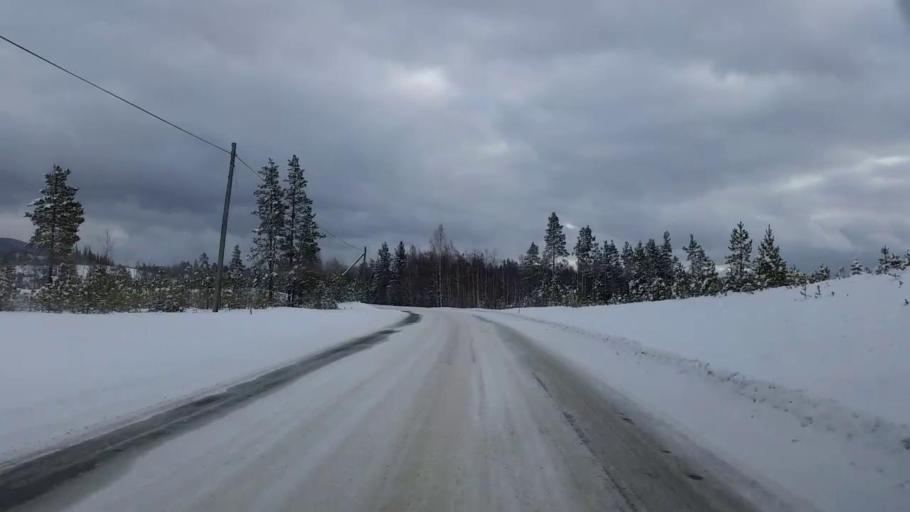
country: SE
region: Jaemtland
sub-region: Harjedalens Kommun
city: Sveg
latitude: 62.1255
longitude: 14.9850
